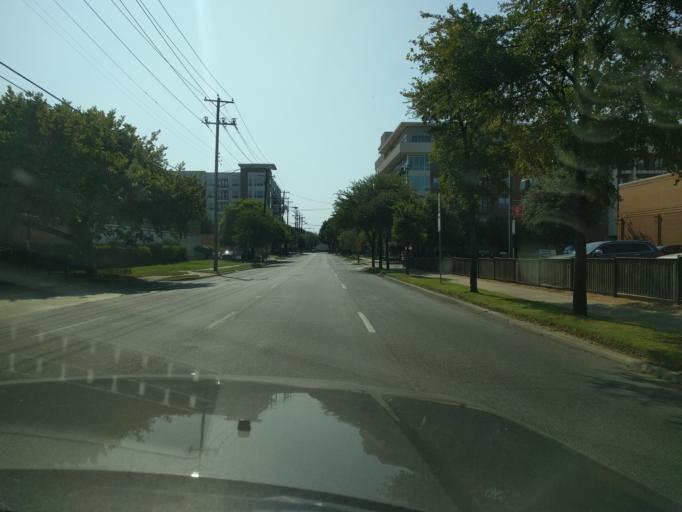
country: US
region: Texas
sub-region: Dallas County
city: Dallas
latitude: 32.8056
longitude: -96.7981
